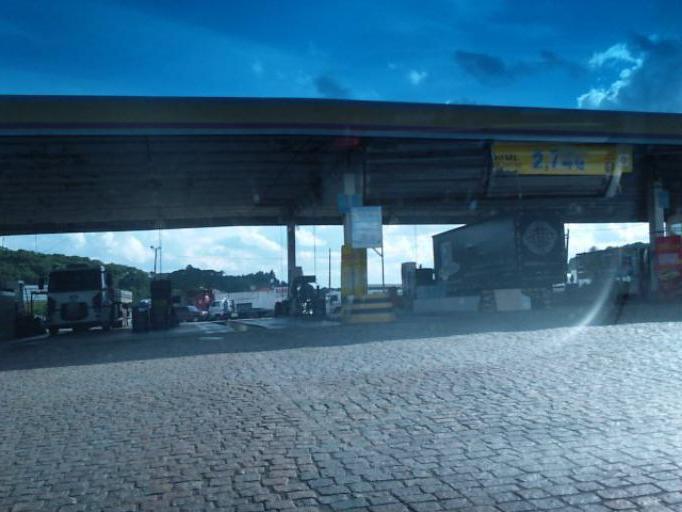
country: BR
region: Parana
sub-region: Campina Grande Do Sul
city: Campina Grande do Sul
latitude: -25.3156
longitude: -49.0186
